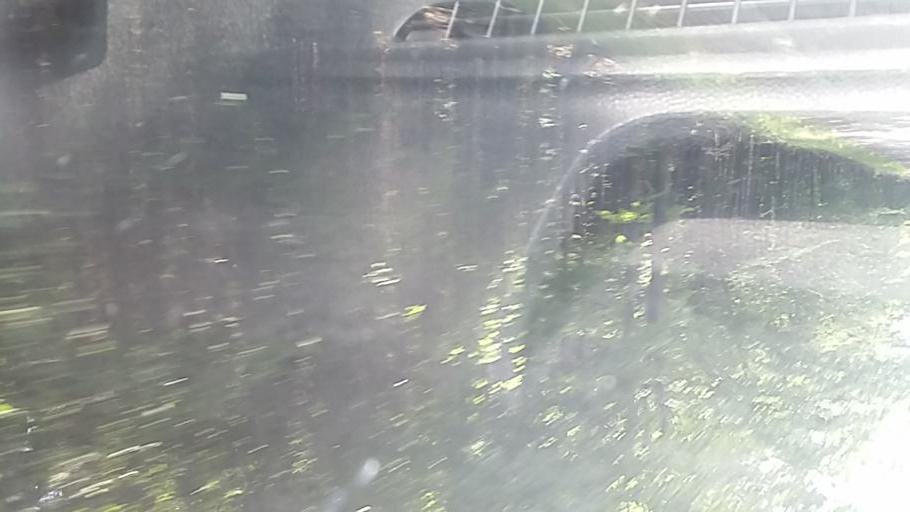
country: HU
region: Nograd
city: Batonyterenye
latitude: 47.8977
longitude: 19.8574
